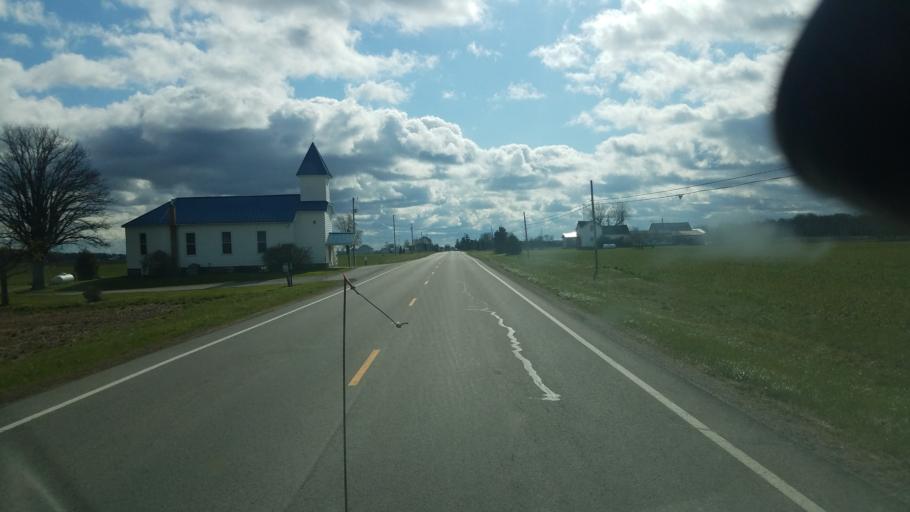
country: US
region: Ohio
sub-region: Hardin County
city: Kenton
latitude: 40.6433
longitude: -83.5016
